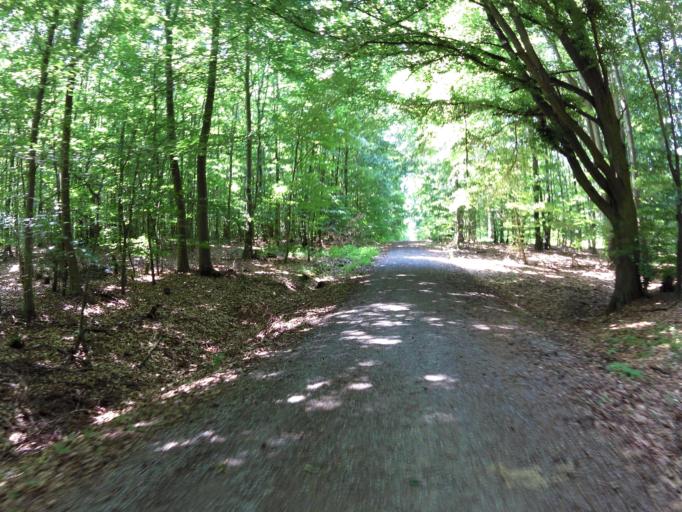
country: DE
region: Bavaria
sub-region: Regierungsbezirk Unterfranken
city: Kist
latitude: 49.7301
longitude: 9.8631
